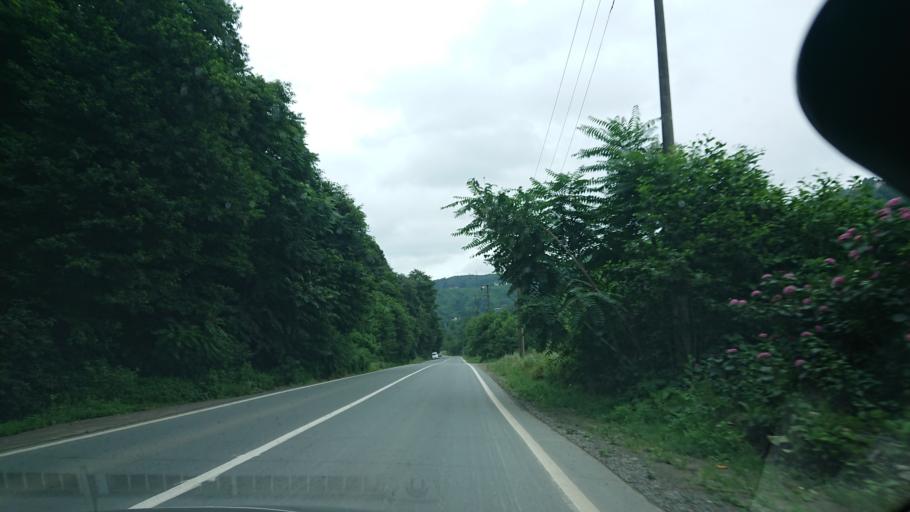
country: TR
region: Rize
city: Gundogdu
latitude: 41.0175
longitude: 40.5705
